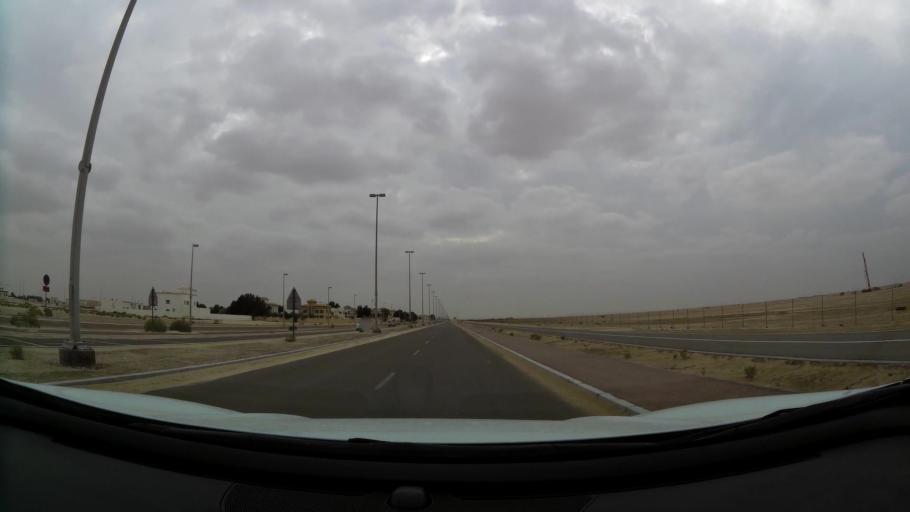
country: AE
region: Abu Dhabi
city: Abu Dhabi
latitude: 24.3817
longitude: 54.6341
